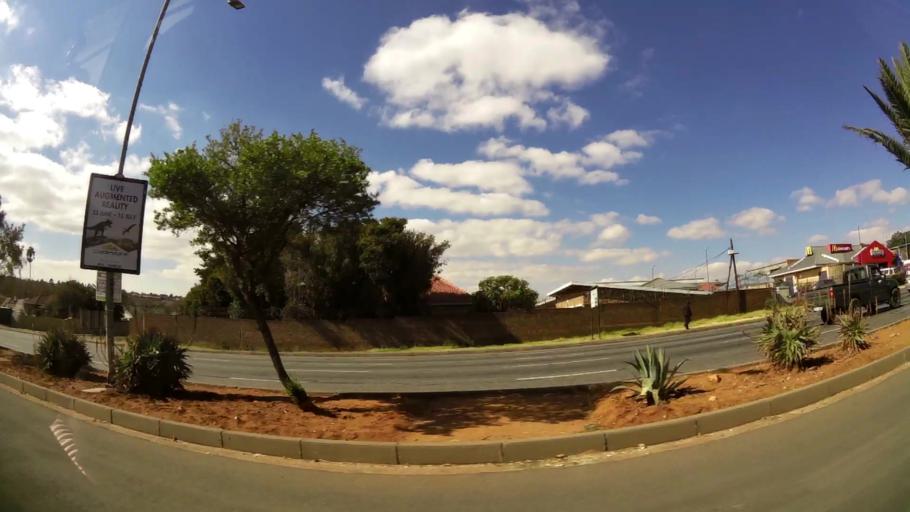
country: ZA
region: Gauteng
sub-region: West Rand District Municipality
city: Krugersdorp
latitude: -26.1063
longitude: 27.7784
